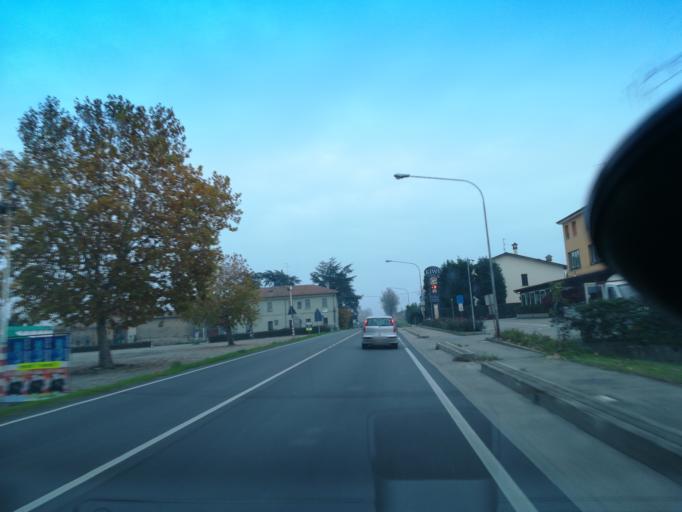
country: IT
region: Emilia-Romagna
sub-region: Provincia di Ravenna
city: Castel Bolognese
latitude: 44.3170
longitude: 11.8063
